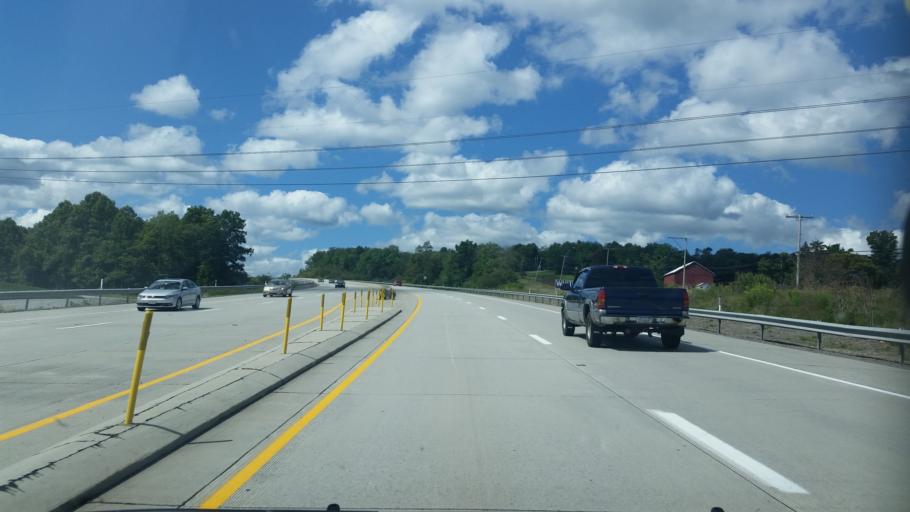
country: US
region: Pennsylvania
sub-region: Indiana County
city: Homer City
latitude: 40.4501
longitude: -79.0599
